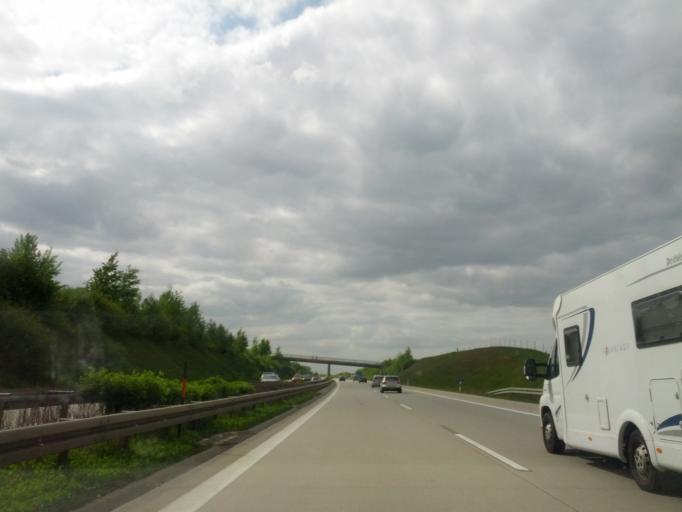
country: DE
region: Saxony
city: Kreischa
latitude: 50.9846
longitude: 13.7839
